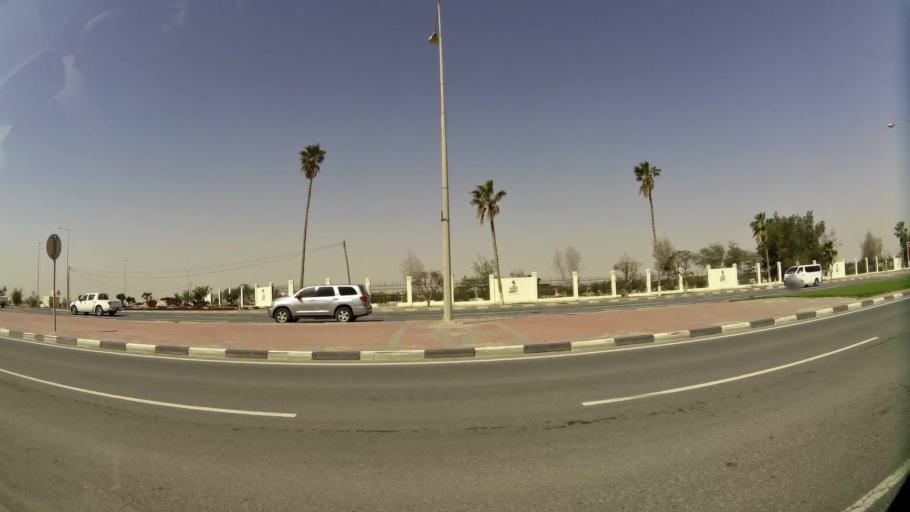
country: QA
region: Baladiyat ad Dawhah
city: Doha
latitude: 25.3589
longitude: 51.4952
